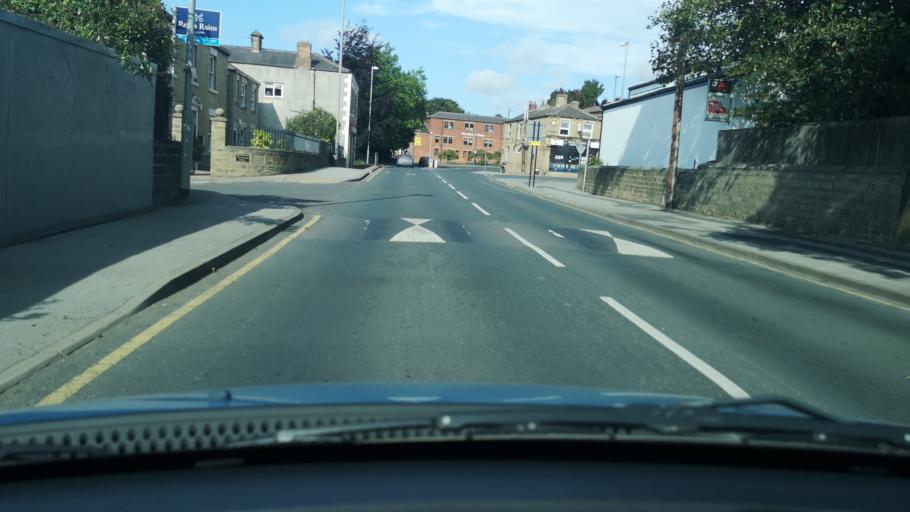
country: GB
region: England
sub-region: City and Borough of Wakefield
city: Ossett
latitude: 53.6773
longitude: -1.5810
